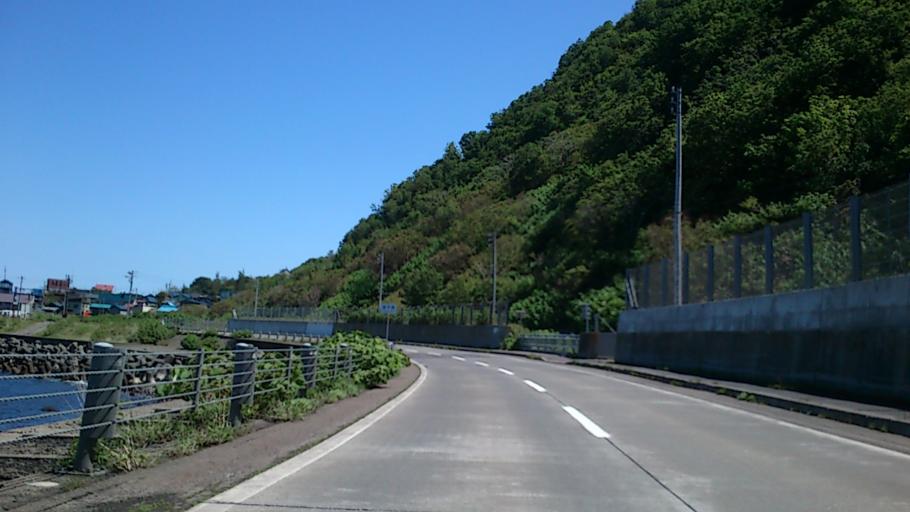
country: JP
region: Hokkaido
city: Rumoi
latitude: 43.7338
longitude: 141.3378
